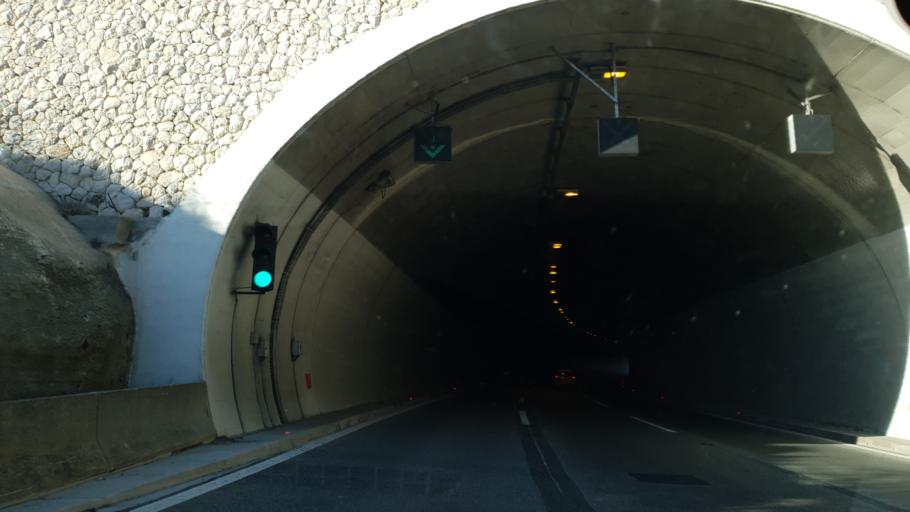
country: HR
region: Splitsko-Dalmatinska
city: Klis
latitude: 43.5628
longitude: 16.5316
